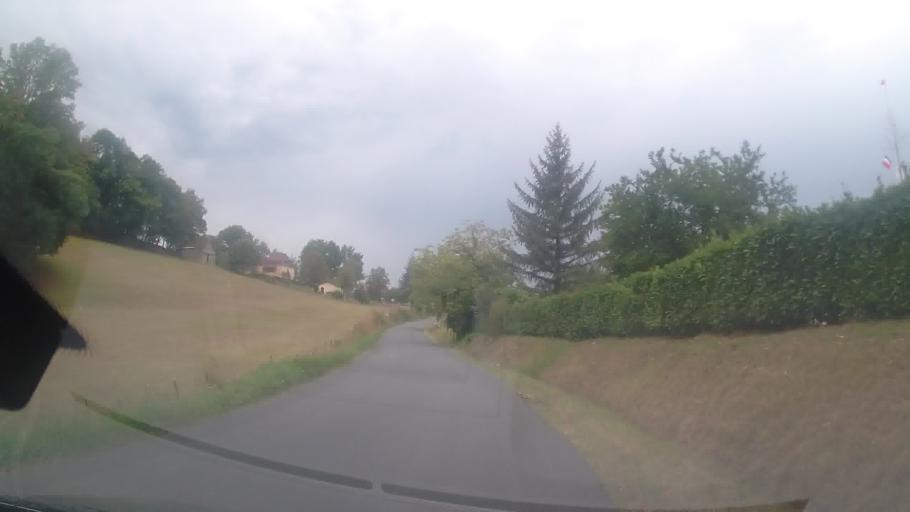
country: FR
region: Aquitaine
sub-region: Departement de la Dordogne
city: Carsac-Aillac
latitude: 44.8382
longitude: 1.2927
